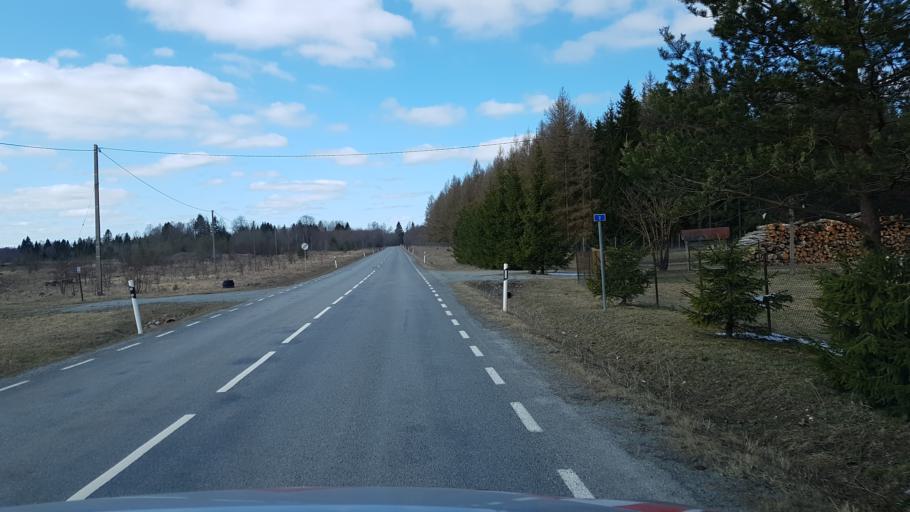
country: EE
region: Laeaene-Virumaa
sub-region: Tapa vald
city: Tapa
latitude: 59.2693
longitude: 25.9296
